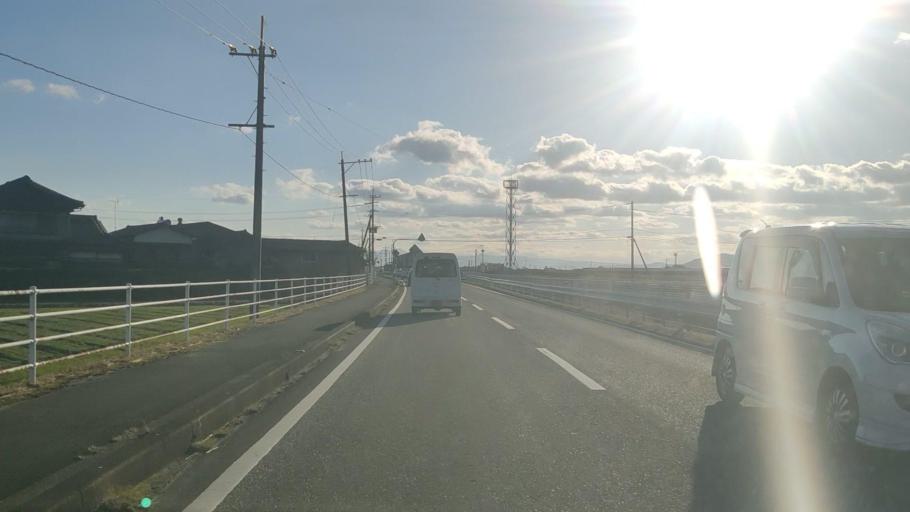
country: JP
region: Saga Prefecture
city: Saga-shi
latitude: 33.2885
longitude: 130.2341
